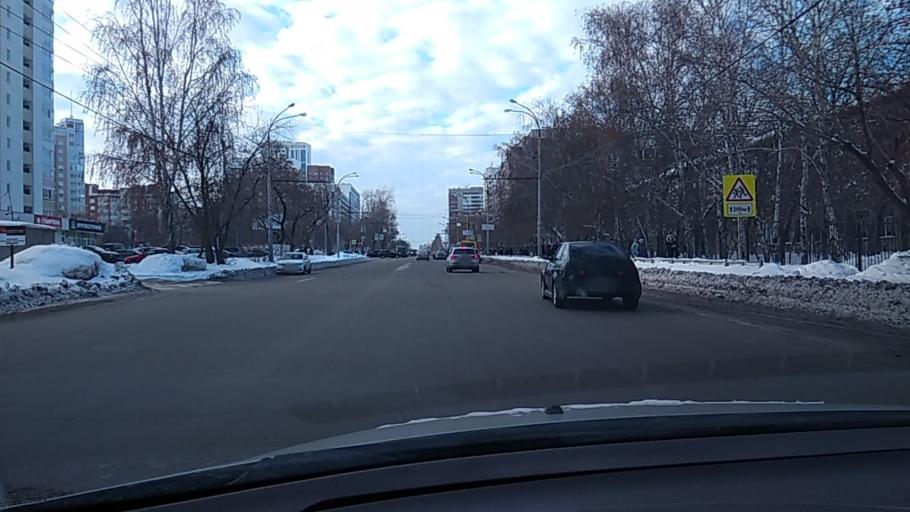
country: RU
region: Sverdlovsk
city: Yekaterinburg
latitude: 56.8081
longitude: 60.6037
